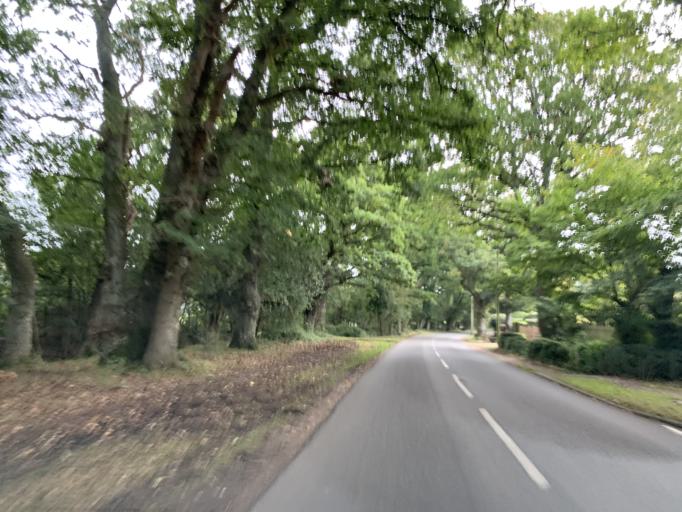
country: GB
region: England
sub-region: Hampshire
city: Brockenhurst
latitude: 50.8230
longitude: -1.5953
